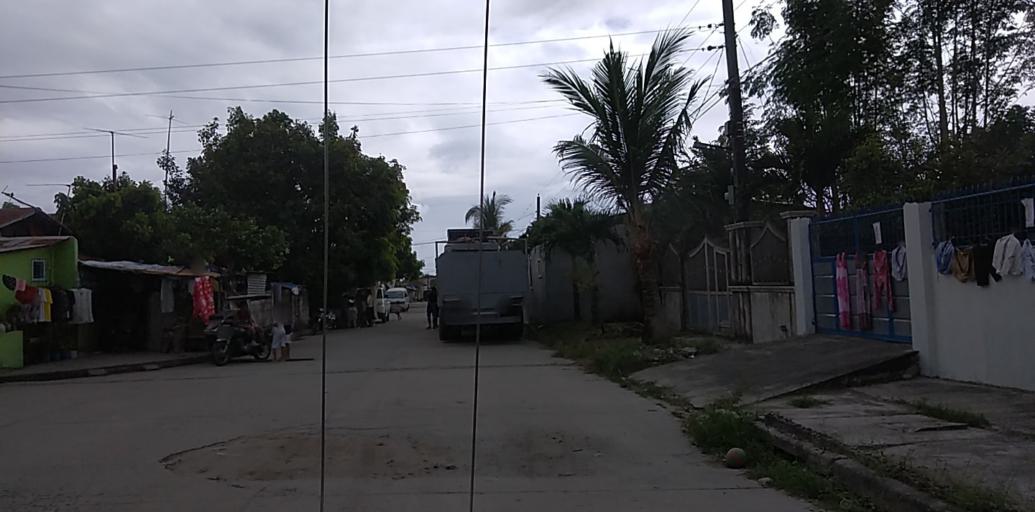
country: PH
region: Central Luzon
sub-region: Province of Pampanga
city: Pio
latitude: 15.0443
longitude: 120.5264
